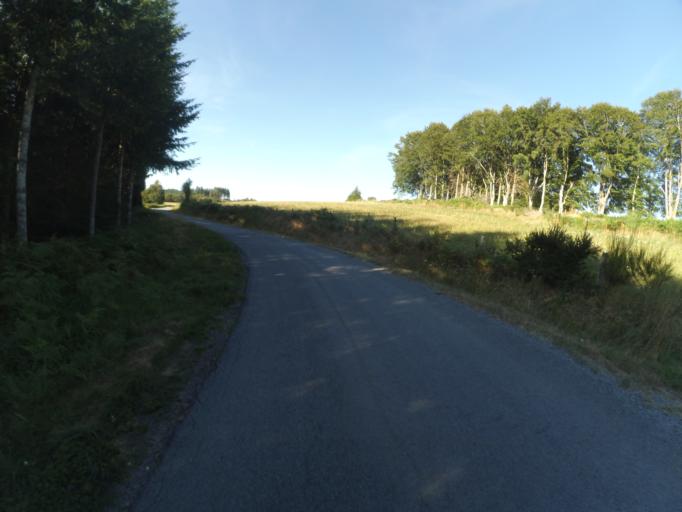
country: FR
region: Limousin
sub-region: Departement de la Creuse
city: Banize
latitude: 45.7551
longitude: 2.0302
